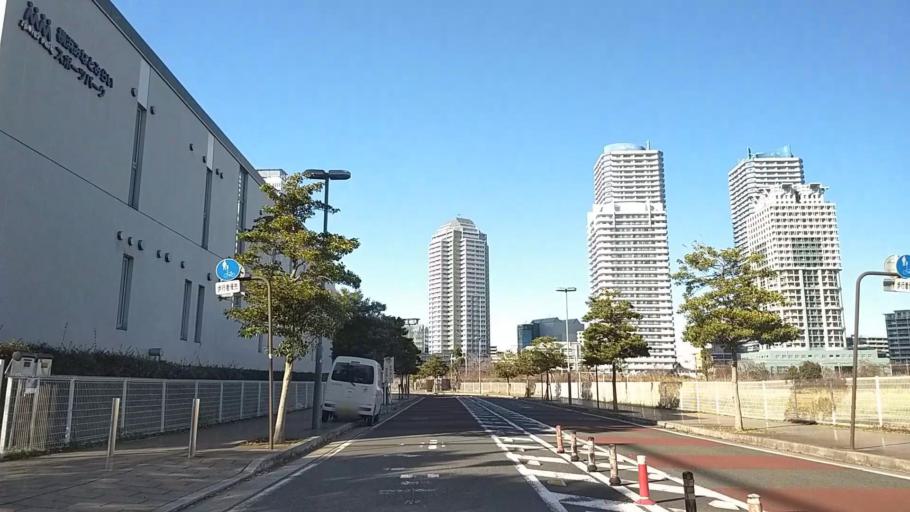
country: JP
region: Kanagawa
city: Yokohama
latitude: 35.4647
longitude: 139.6317
